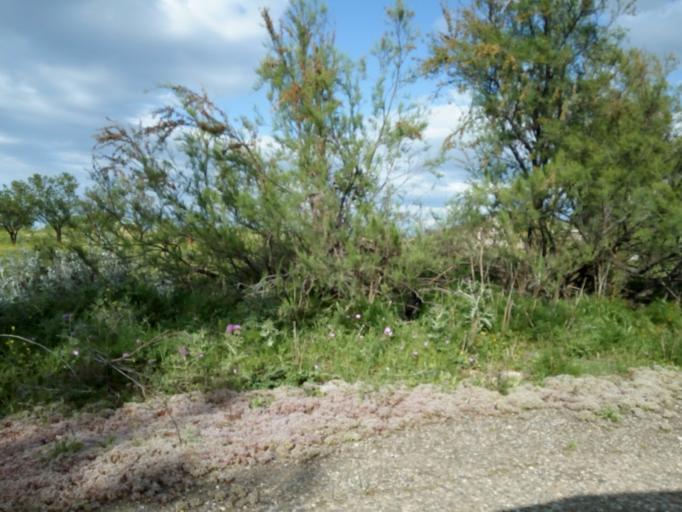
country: DZ
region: Tipaza
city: El Affroun
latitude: 36.3753
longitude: 2.5179
